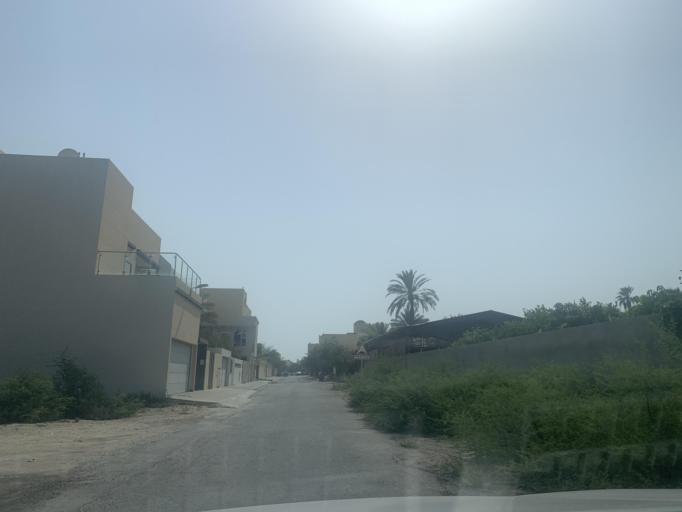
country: BH
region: Manama
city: Jidd Hafs
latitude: 26.2215
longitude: 50.4728
